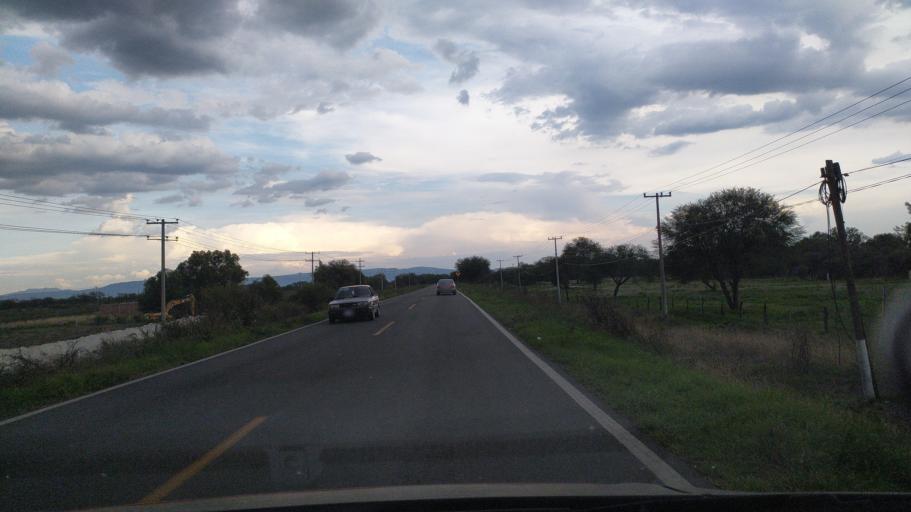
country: MX
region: Guanajuato
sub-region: San Francisco del Rincon
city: San Ignacio de Hidalgo
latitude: 20.8238
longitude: -101.9029
